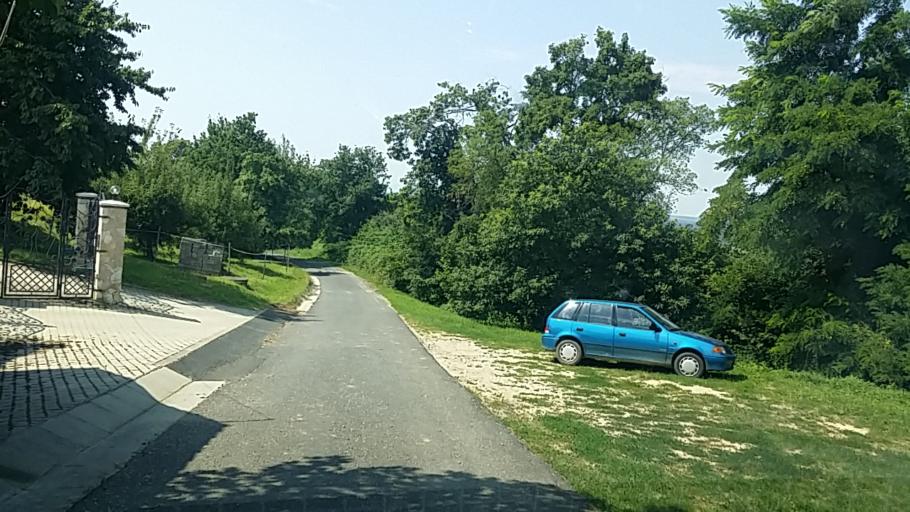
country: HR
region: Medimurska
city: Domasinec
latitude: 46.5099
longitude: 16.6258
